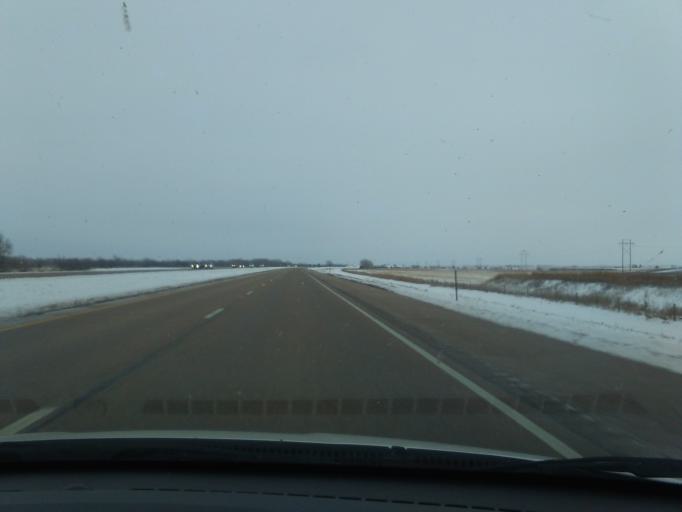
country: US
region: Nebraska
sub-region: Keith County
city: Ogallala
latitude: 41.0918
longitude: -101.8342
